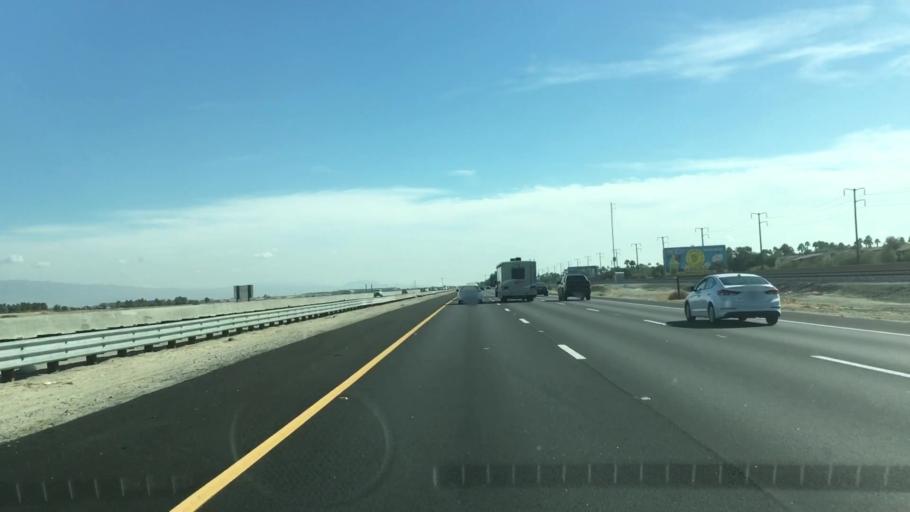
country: US
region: California
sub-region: Riverside County
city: Indian Wells
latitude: 33.7787
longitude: -116.3424
